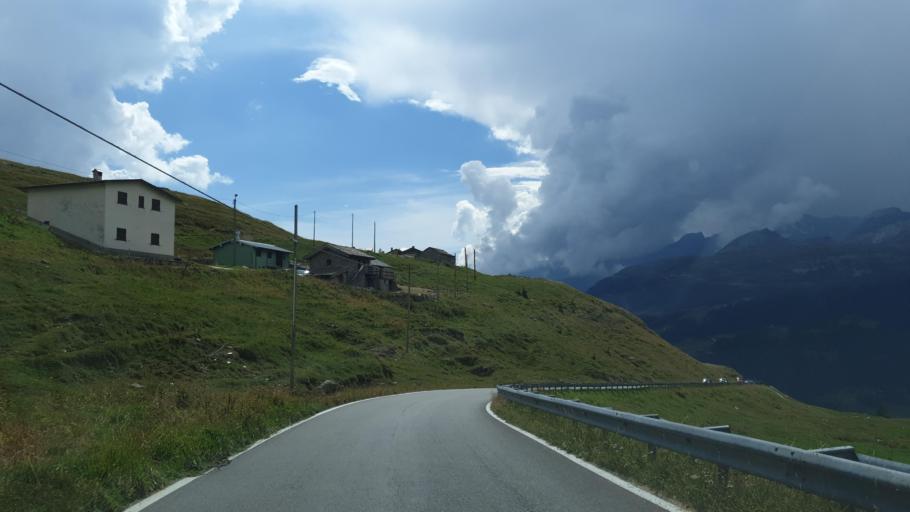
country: IT
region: Lombardy
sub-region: Provincia di Sondrio
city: Campodolcino
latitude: 46.4585
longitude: 9.3383
